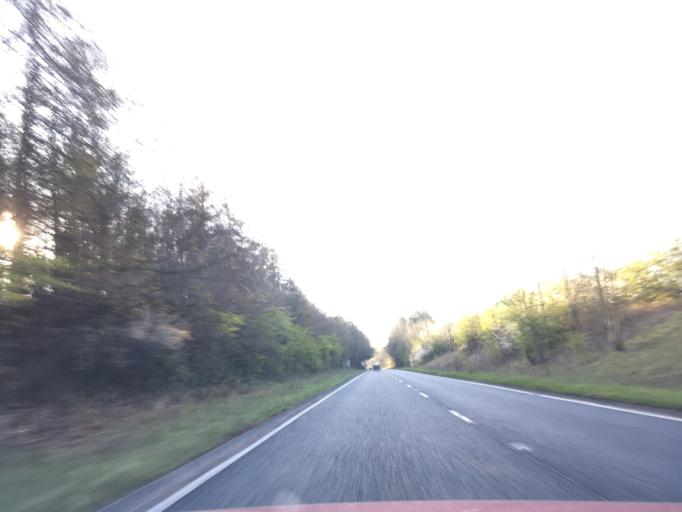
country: GB
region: England
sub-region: Gloucestershire
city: Northleach
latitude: 51.8296
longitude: -1.8143
